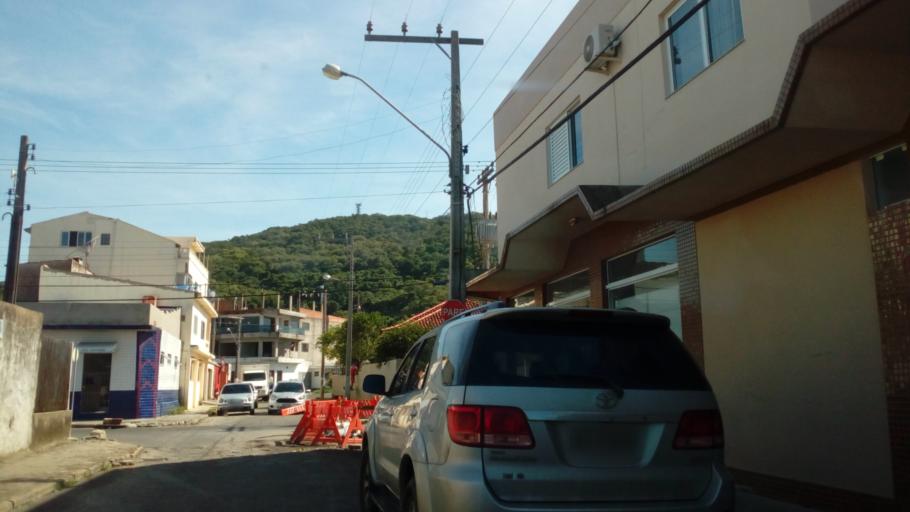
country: BR
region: Santa Catarina
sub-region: Laguna
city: Laguna
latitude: -28.4935
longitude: -48.7816
